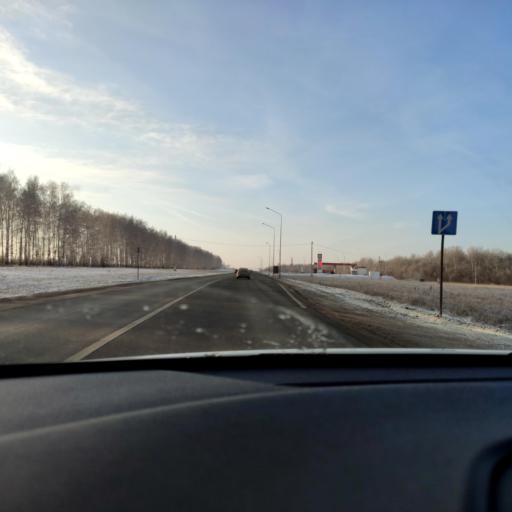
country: RU
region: Tatarstan
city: Vysokaya Gora
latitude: 55.9824
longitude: 49.4841
